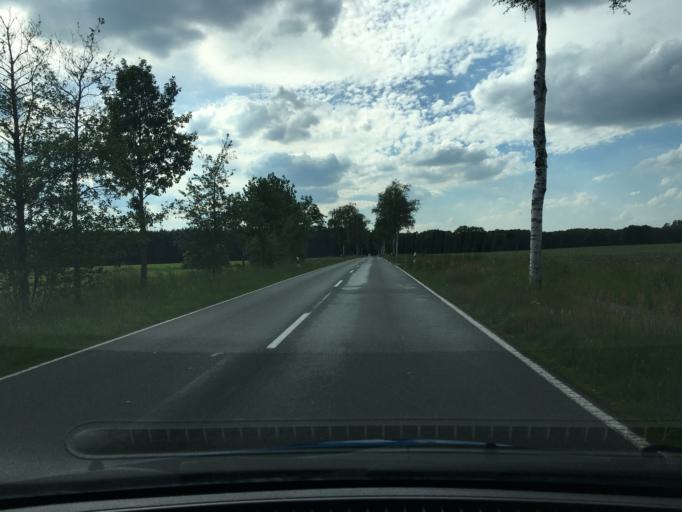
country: DE
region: Lower Saxony
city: Otter
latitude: 53.2528
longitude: 9.7622
